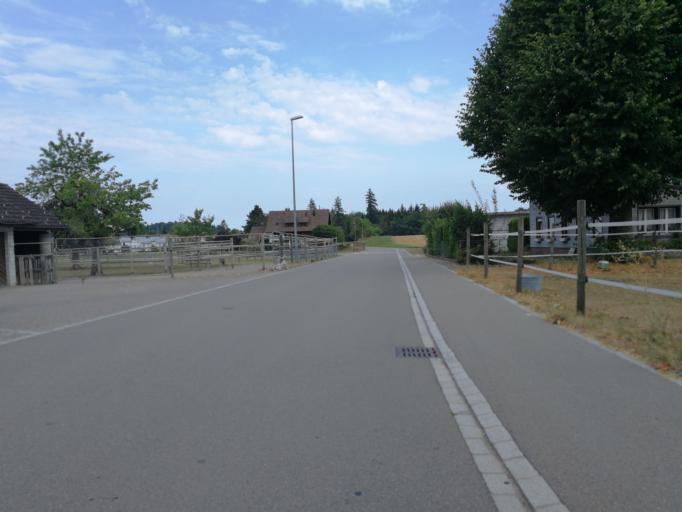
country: CH
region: Zurich
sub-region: Bezirk Hinwil
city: Wetzikon / Robenhausen
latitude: 47.3298
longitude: 8.7690
